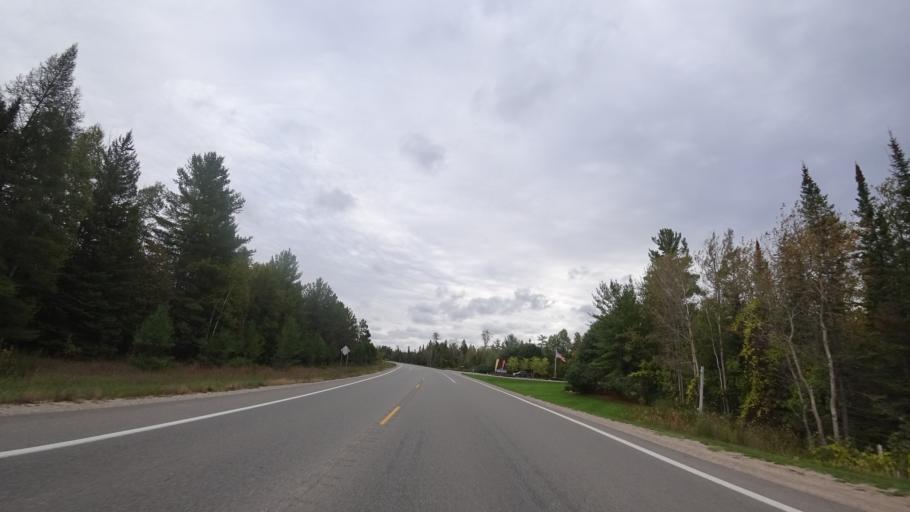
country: US
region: Michigan
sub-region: Charlevoix County
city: Boyne City
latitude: 45.1583
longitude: -84.9197
